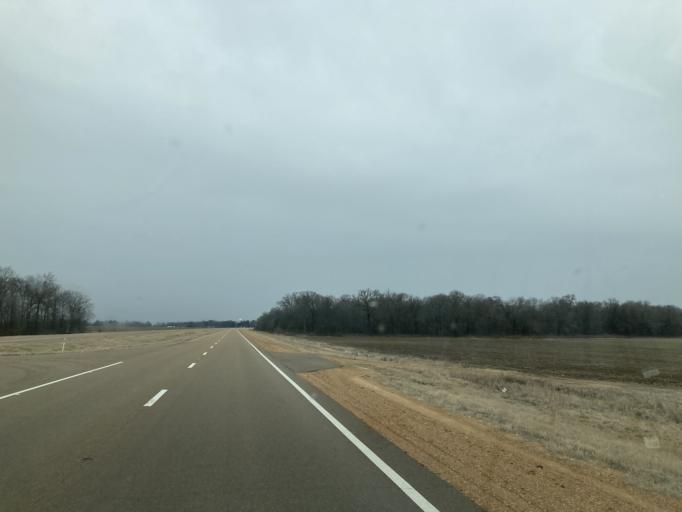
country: US
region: Mississippi
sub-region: Humphreys County
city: Belzoni
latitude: 33.0786
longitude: -90.4799
